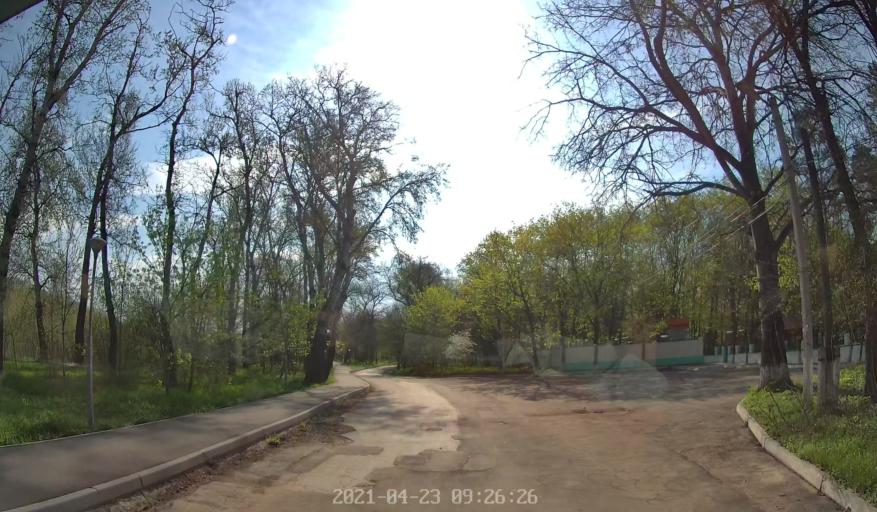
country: MD
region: Chisinau
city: Vadul lui Voda
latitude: 47.0870
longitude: 29.0940
